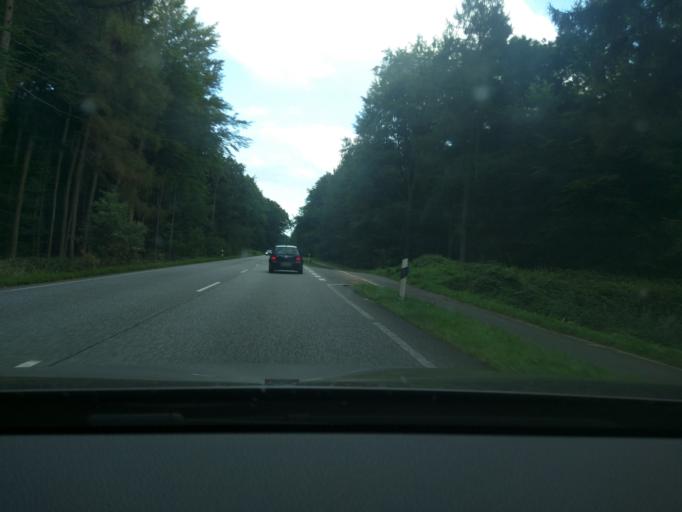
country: DE
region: Schleswig-Holstein
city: Brunstorf
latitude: 53.5336
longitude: 10.4310
